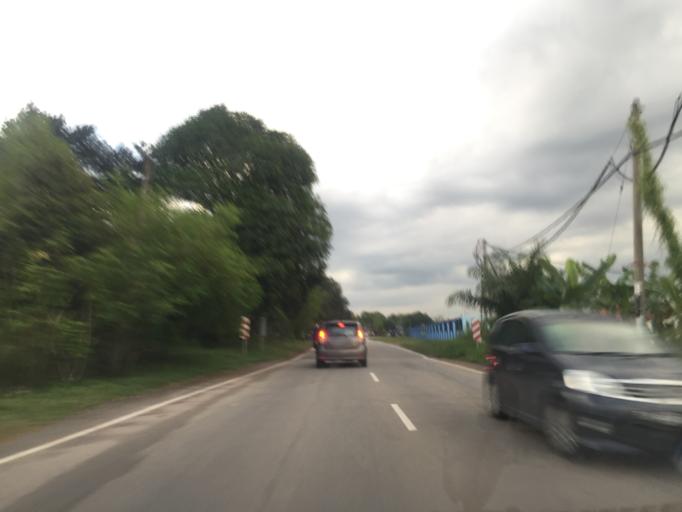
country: MY
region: Kedah
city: Sungai Petani
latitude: 5.5718
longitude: 100.5028
